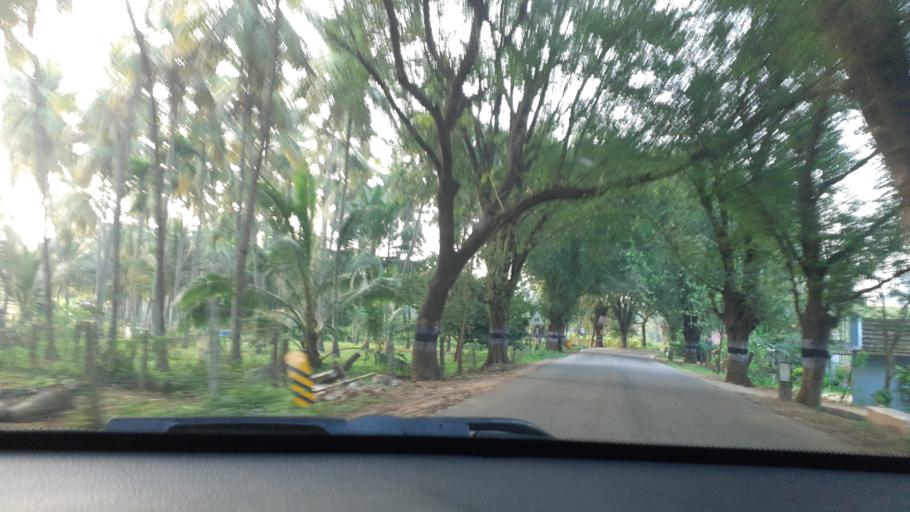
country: IN
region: Tamil Nadu
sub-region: Dindigul
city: Ayakudi
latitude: 10.4151
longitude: 77.5375
